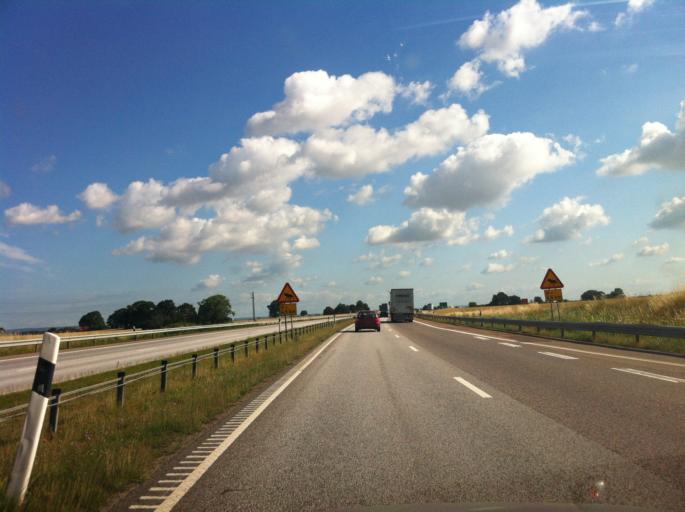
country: SE
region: Skane
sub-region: Angelholms Kommun
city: AEngelholm
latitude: 56.1969
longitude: 12.8607
